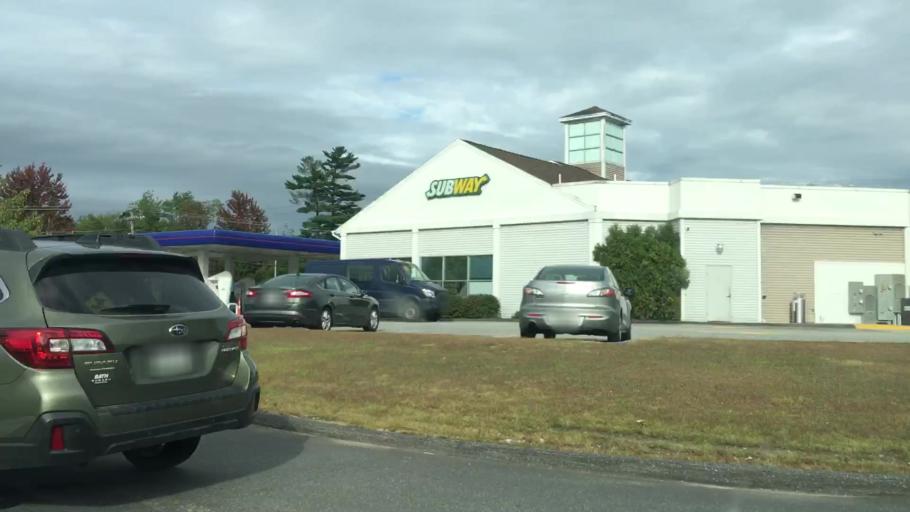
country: US
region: Maine
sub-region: Sagadahoc County
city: Topsham
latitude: 43.9369
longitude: -69.9720
